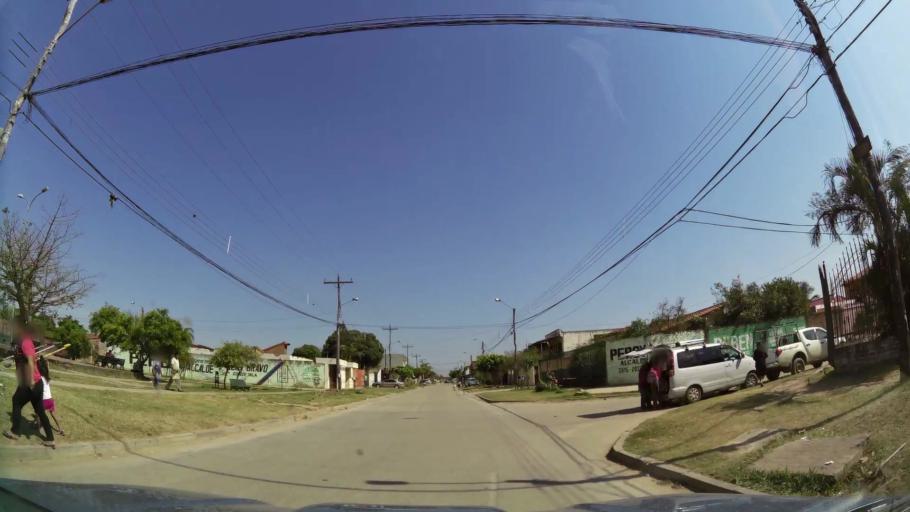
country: BO
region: Santa Cruz
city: Santa Cruz de la Sierra
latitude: -17.7466
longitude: -63.1457
